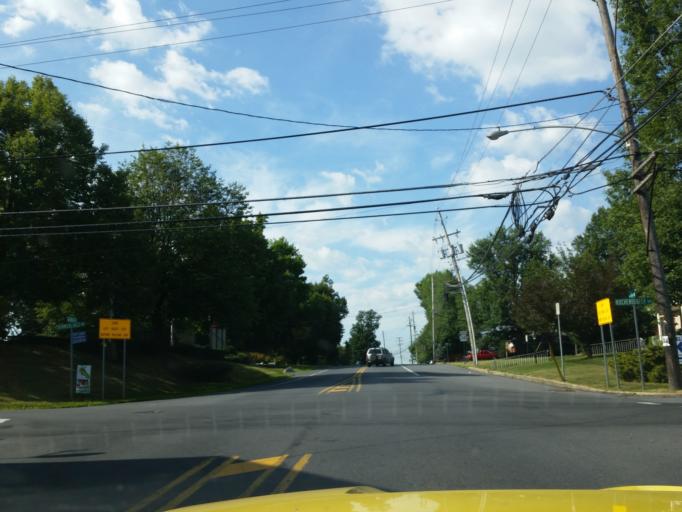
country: US
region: Pennsylvania
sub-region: Lebanon County
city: Sand Hill
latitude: 40.3662
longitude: -76.4171
